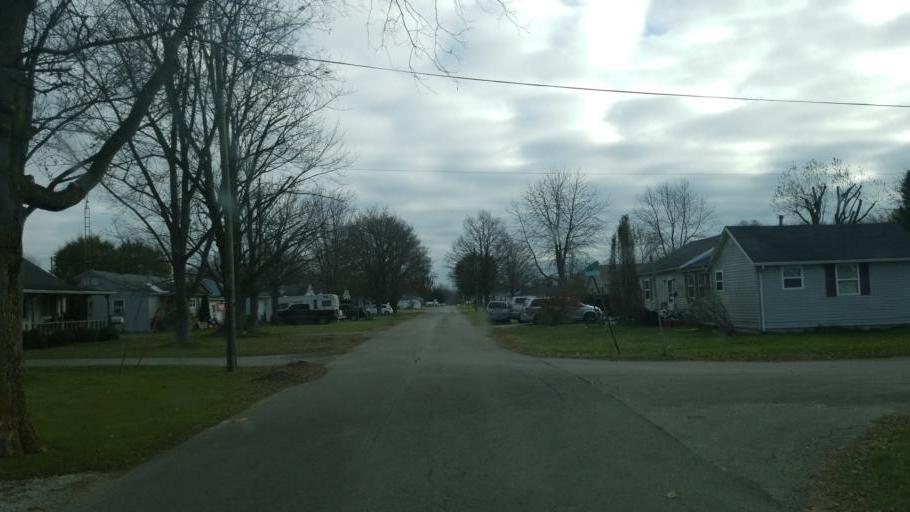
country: US
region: Ohio
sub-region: Hardin County
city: Kenton
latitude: 40.6540
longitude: -83.6199
